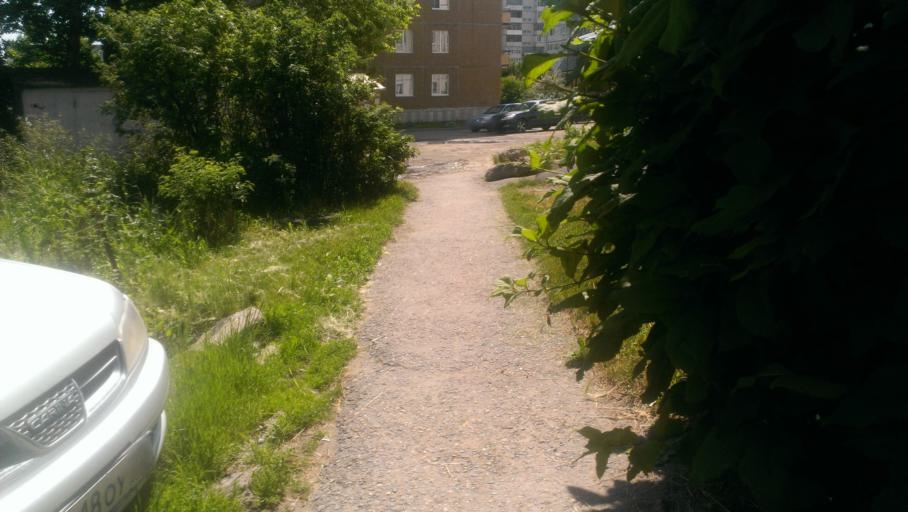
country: RU
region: Altai Krai
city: Novosilikatnyy
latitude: 53.3422
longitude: 83.6734
